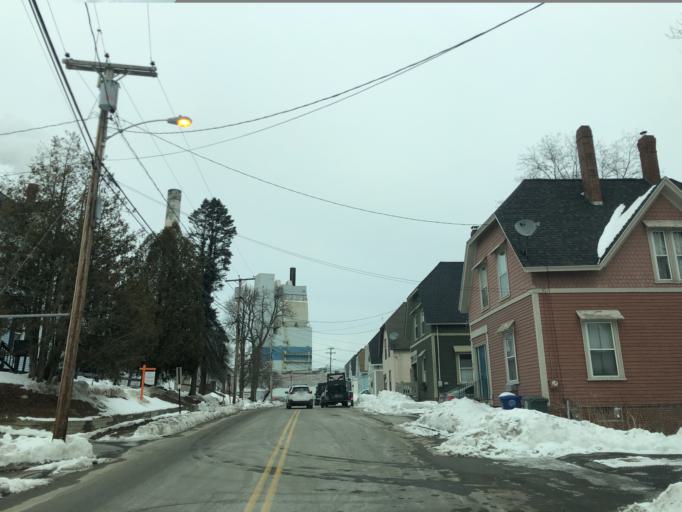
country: US
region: Maine
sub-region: Cumberland County
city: Westbrook
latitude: 43.6828
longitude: -70.3549
